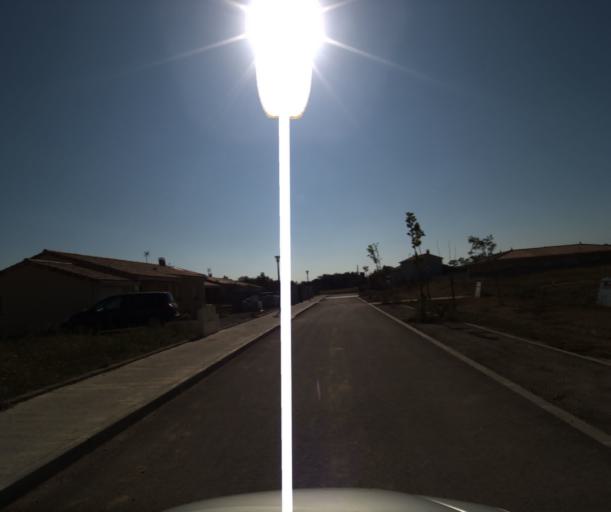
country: FR
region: Midi-Pyrenees
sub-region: Departement de la Haute-Garonne
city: Eaunes
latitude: 43.4359
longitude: 1.3668
